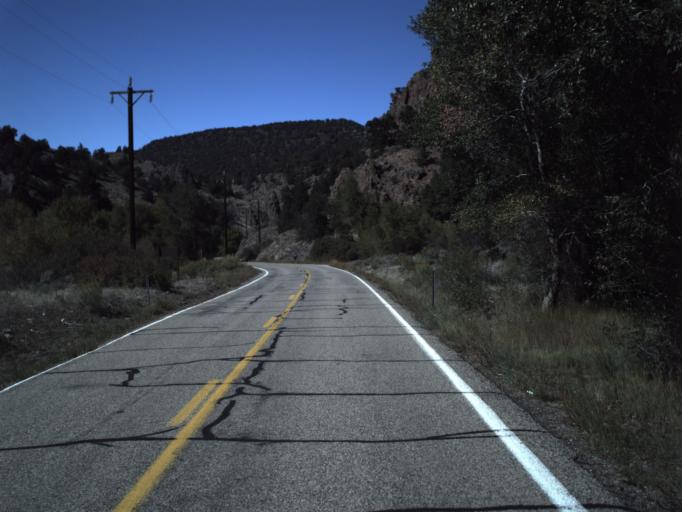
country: US
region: Utah
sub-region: Beaver County
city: Beaver
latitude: 38.2683
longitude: -112.5495
